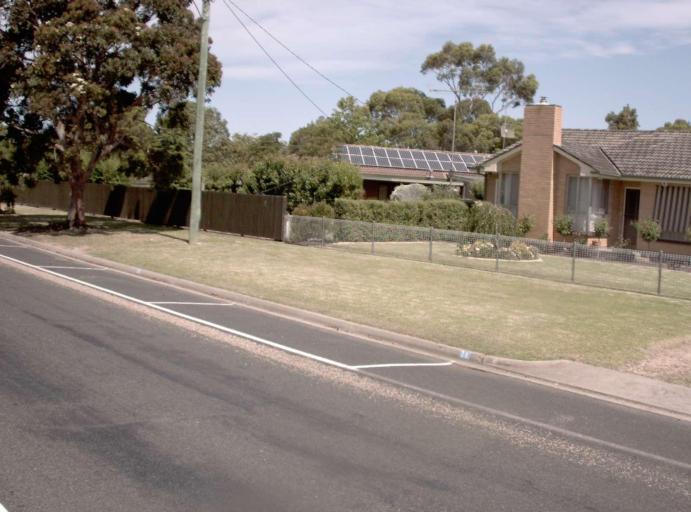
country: AU
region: Victoria
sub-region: Wellington
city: Sale
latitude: -37.9640
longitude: 147.0823
